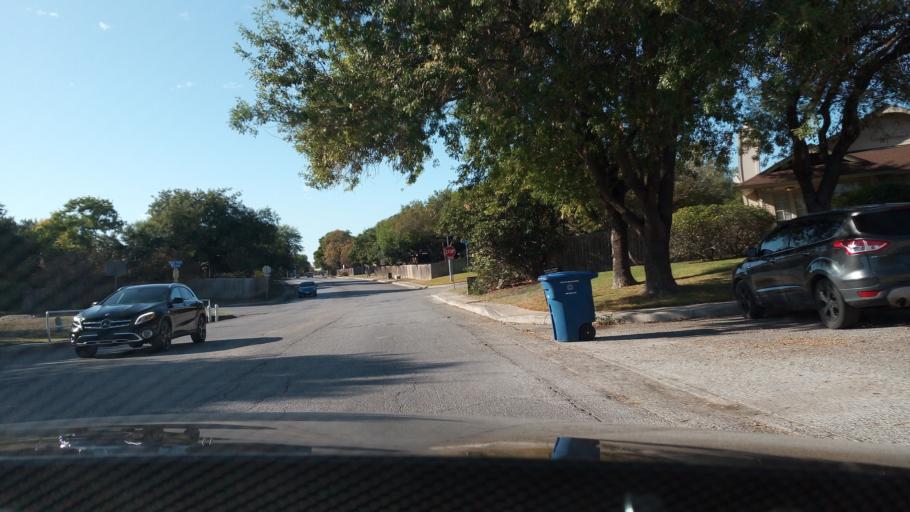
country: US
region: Texas
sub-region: Bexar County
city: Windcrest
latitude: 29.5551
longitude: -98.4314
